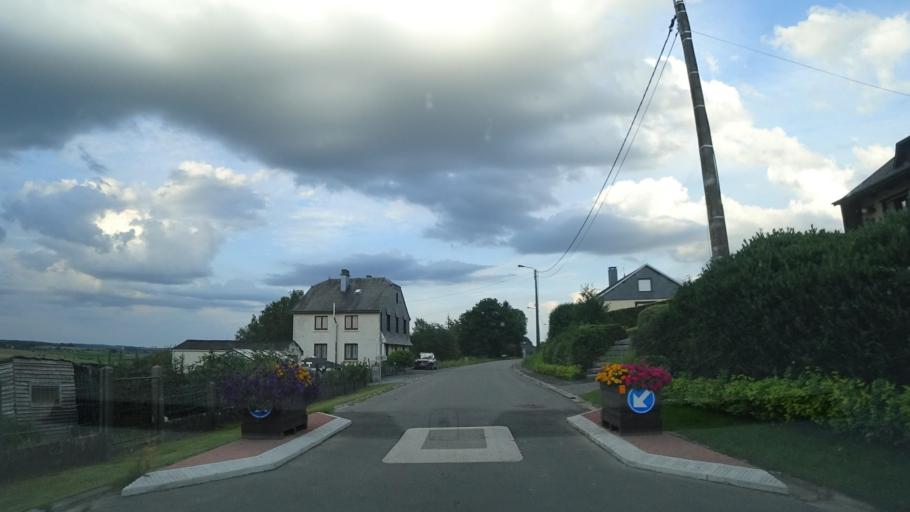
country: BE
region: Wallonia
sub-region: Province du Luxembourg
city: Bertrix
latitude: 49.8170
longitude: 5.3247
